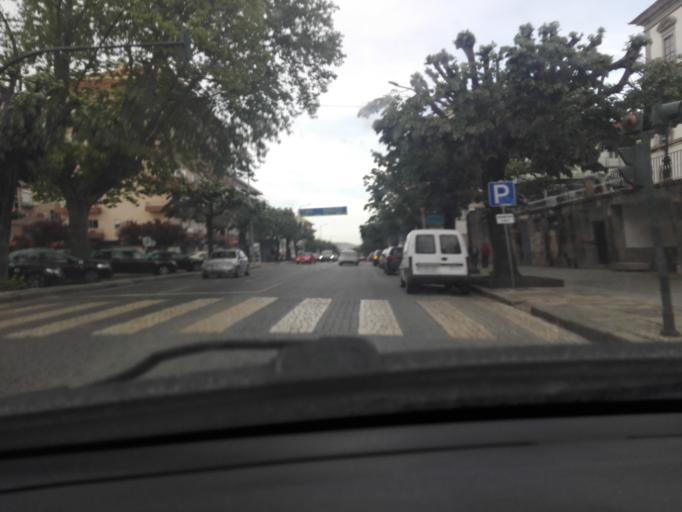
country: PT
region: Castelo Branco
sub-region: Concelho do Fundao
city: Fundao
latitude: 40.1380
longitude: -7.5009
